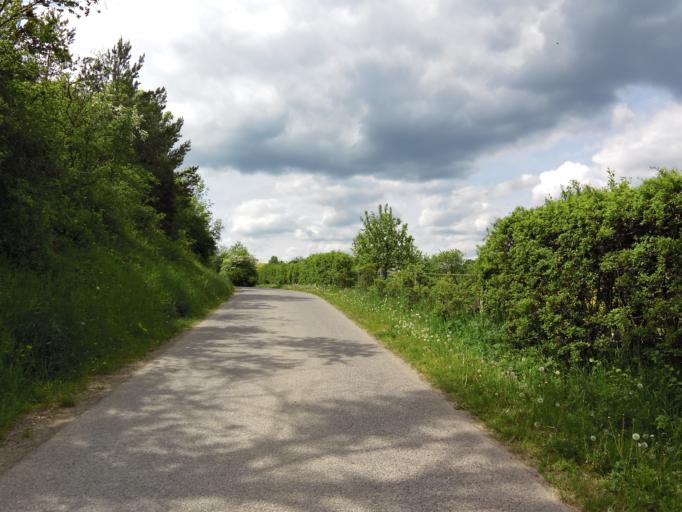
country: DE
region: Thuringia
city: Ifta
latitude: 51.0665
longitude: 10.1699
